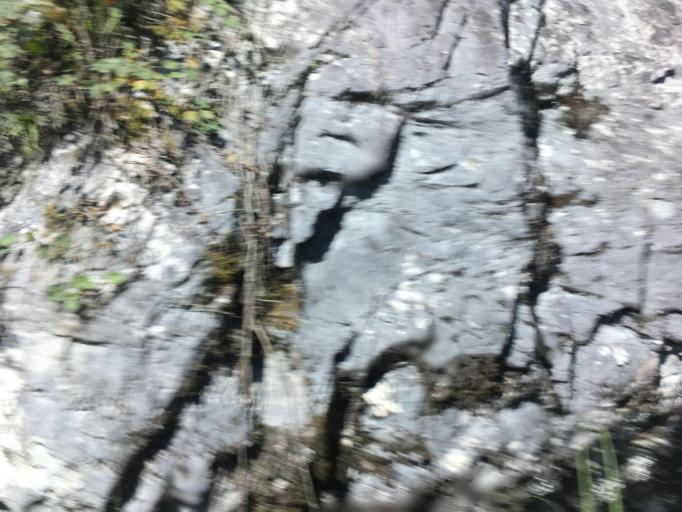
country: TW
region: Taiwan
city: Daxi
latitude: 24.6094
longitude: 121.4591
